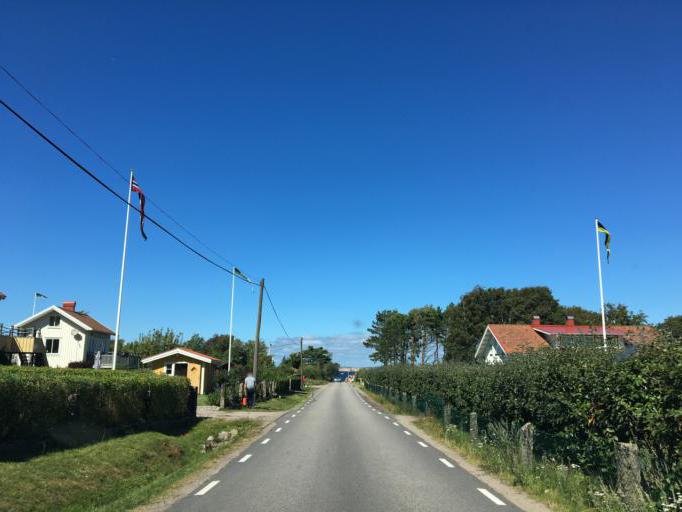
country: SE
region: Vaestra Goetaland
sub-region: Sotenas Kommun
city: Hunnebostrand
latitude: 58.4366
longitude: 11.2667
